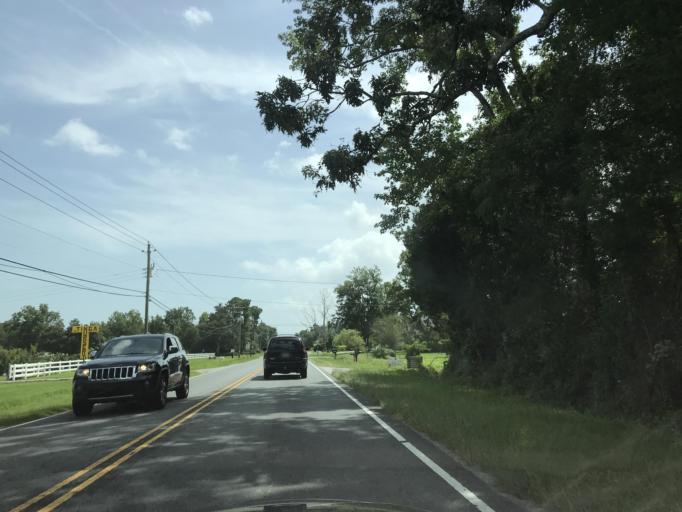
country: US
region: North Carolina
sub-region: New Hanover County
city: Wrightsboro
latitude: 34.2993
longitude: -77.9216
